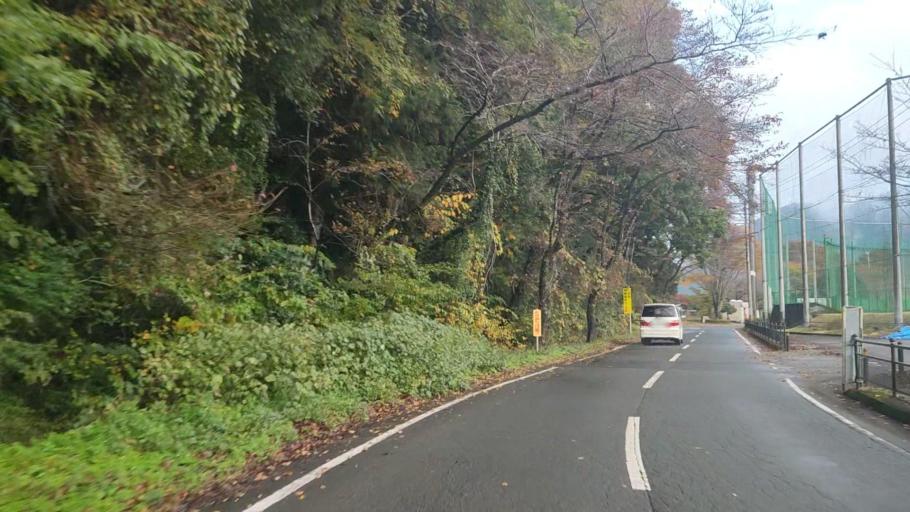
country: JP
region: Shizuoka
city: Fujinomiya
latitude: 35.2772
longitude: 138.4570
